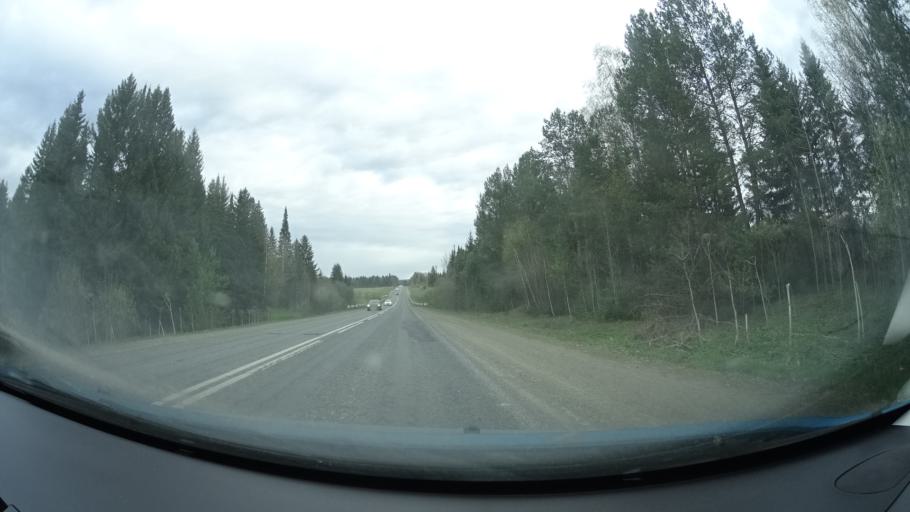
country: RU
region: Perm
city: Yugo-Kamskiy
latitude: 57.6750
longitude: 55.5808
